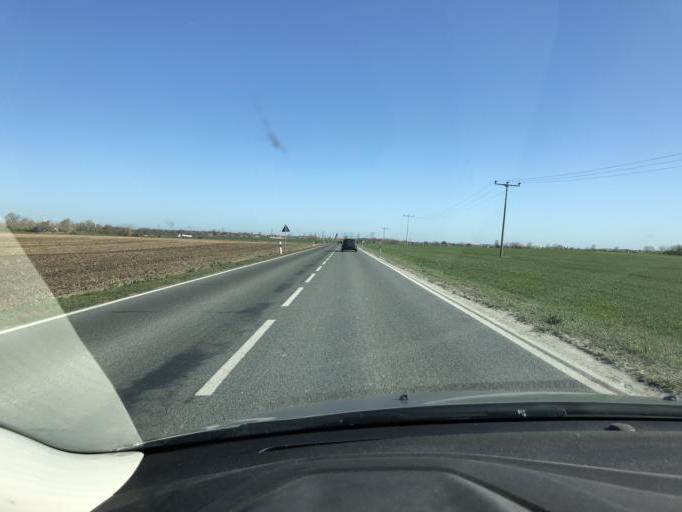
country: DE
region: Saxony-Anhalt
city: Forderstedt
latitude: 51.8804
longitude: 11.6202
